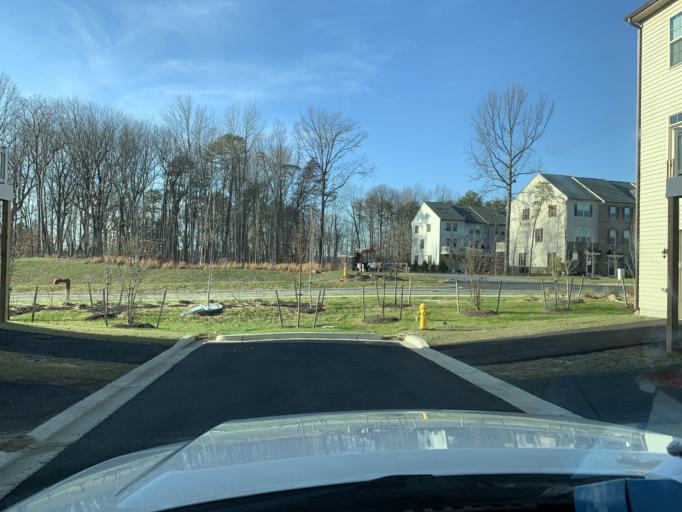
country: US
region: Maryland
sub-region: Anne Arundel County
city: Fort Meade
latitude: 39.1304
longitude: -76.7513
